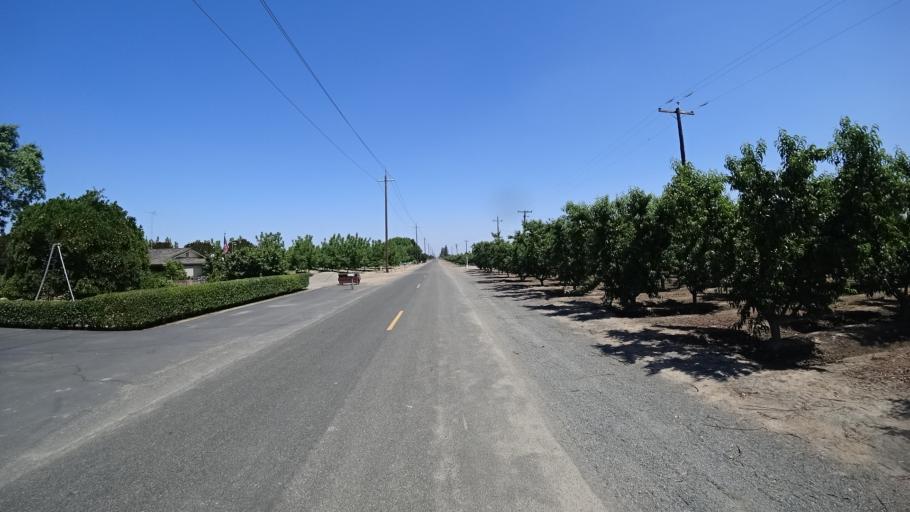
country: US
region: California
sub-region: Fresno County
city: Kingsburg
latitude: 36.4681
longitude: -119.5823
